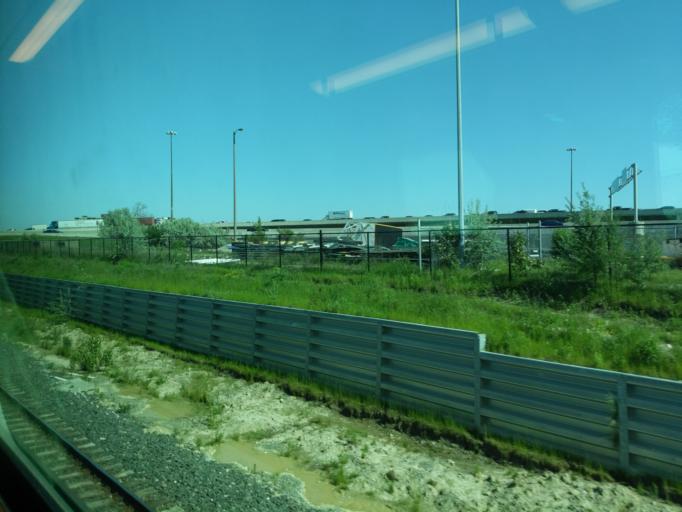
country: CA
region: Ontario
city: Etobicoke
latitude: 43.7064
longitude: -79.5592
